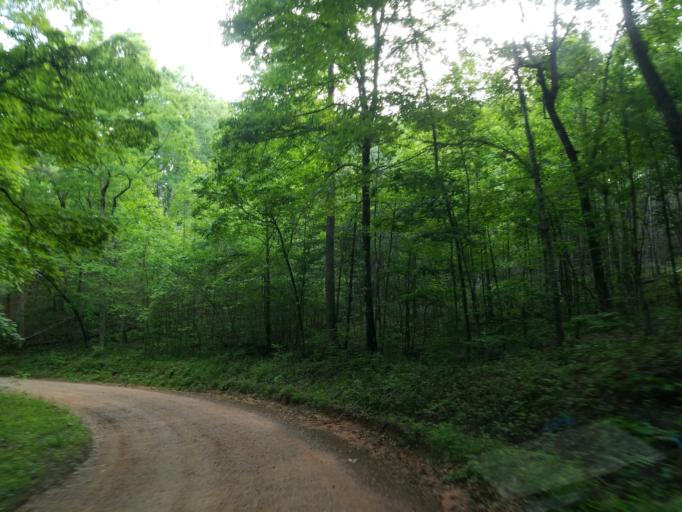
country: US
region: Georgia
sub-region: Lumpkin County
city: Dahlonega
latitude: 34.5959
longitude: -84.1163
